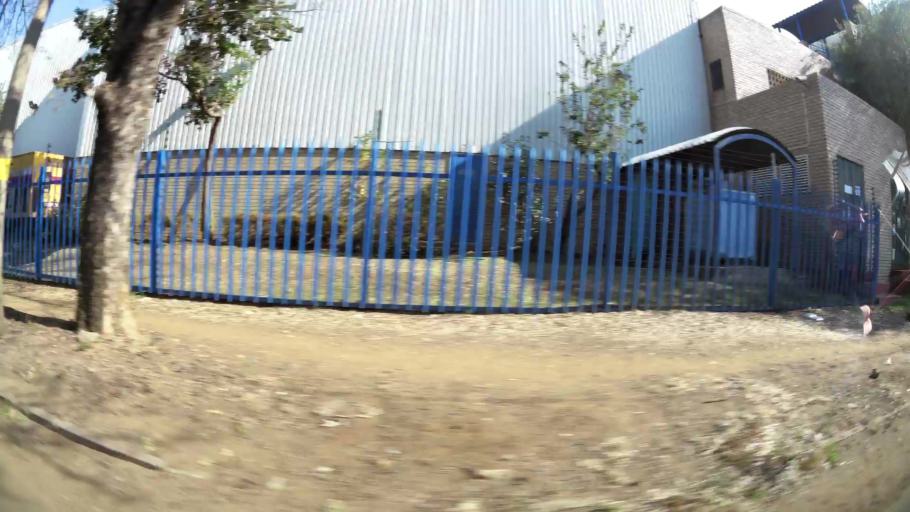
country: ZA
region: Gauteng
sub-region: City of Johannesburg Metropolitan Municipality
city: Modderfontein
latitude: -26.1314
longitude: 28.2170
